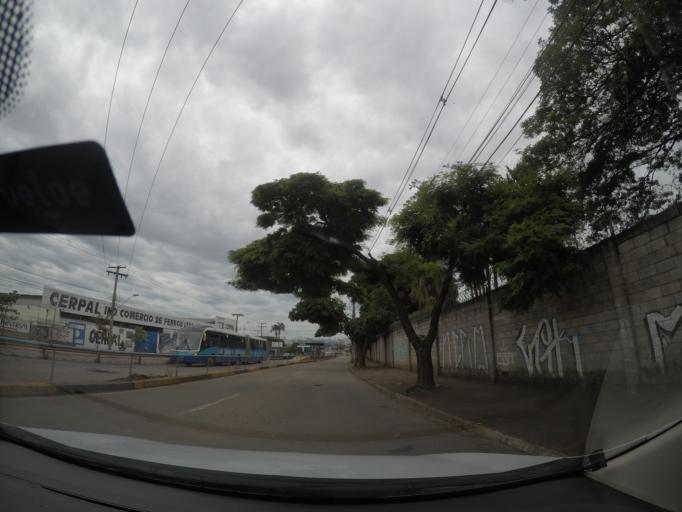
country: BR
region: Goias
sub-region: Goiania
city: Goiania
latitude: -16.6611
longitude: -49.3248
